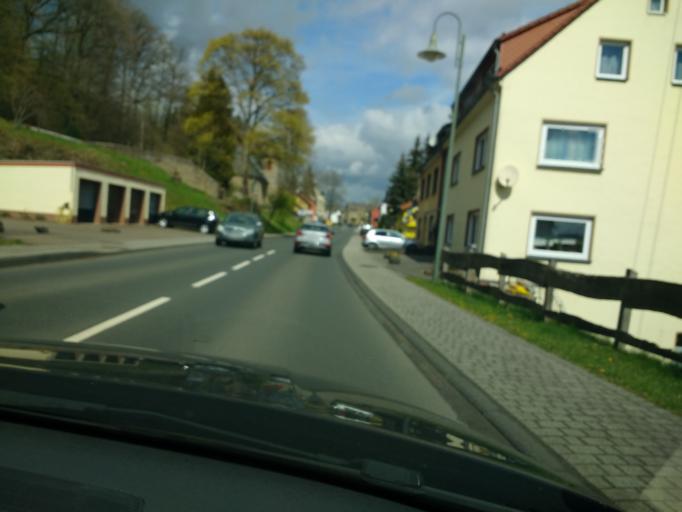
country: DE
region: Rheinland-Pfalz
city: Junkerath
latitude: 50.3404
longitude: 6.5838
